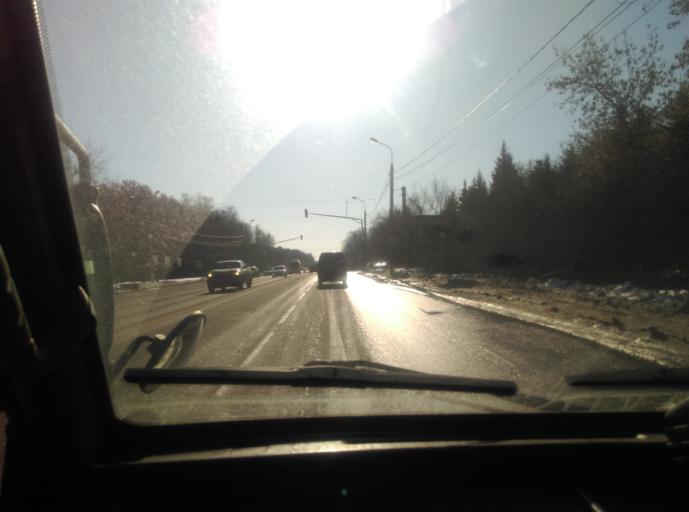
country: RU
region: Moskovskaya
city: Domodedovo
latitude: 55.4209
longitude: 37.7759
